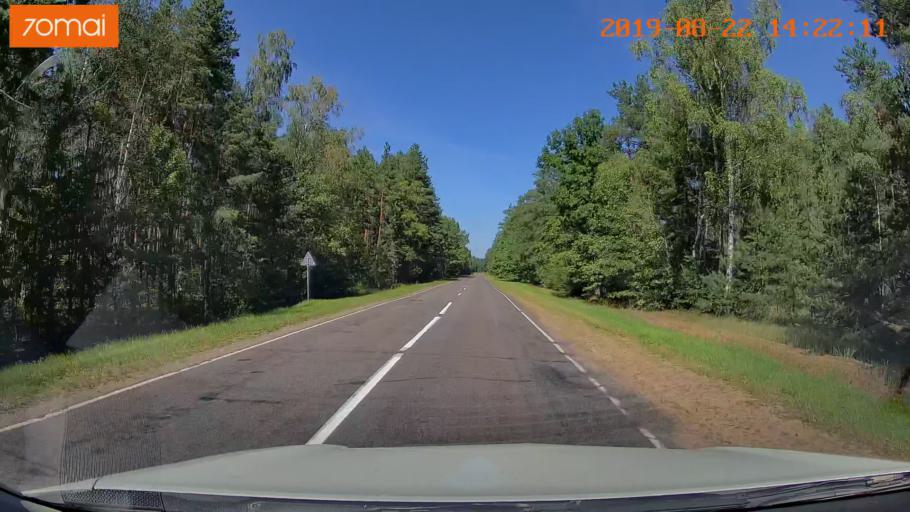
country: BY
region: Mogilev
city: Asipovichy
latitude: 53.2732
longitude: 28.5684
